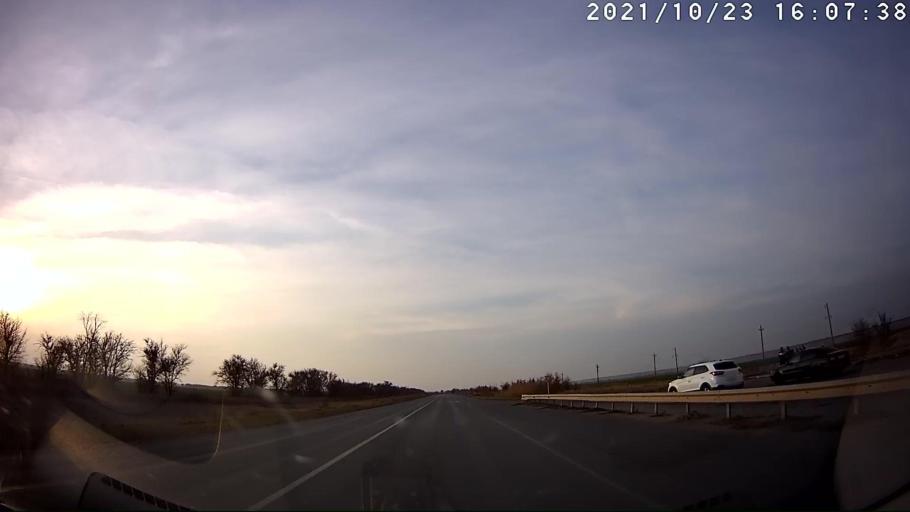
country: RU
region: Volgograd
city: Kotel'nikovo
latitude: 47.9352
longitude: 43.7326
